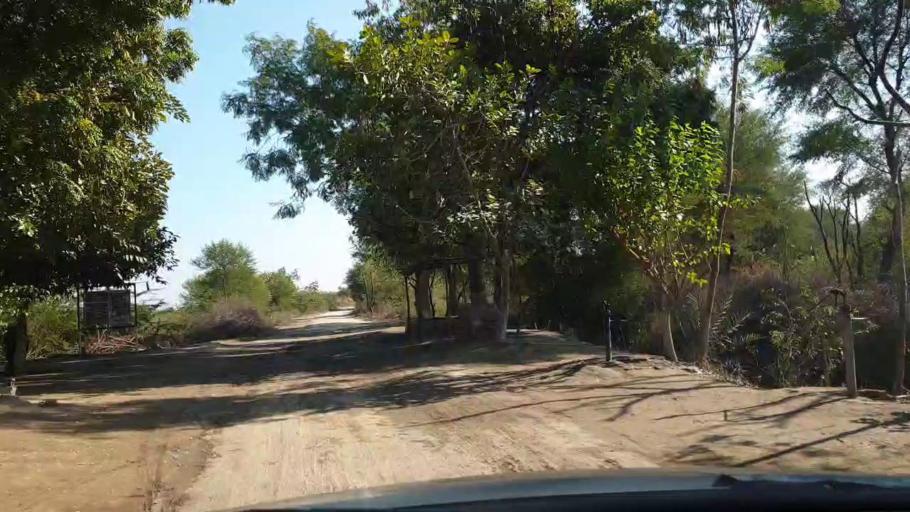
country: PK
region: Sindh
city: Jhol
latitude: 25.9188
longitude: 68.9629
